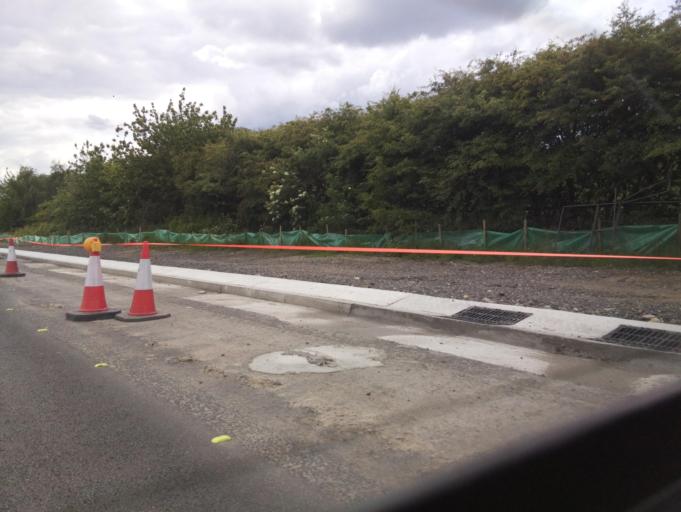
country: GB
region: England
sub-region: Newcastle upon Tyne
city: Hazlerigg
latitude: 55.0251
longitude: -1.6450
